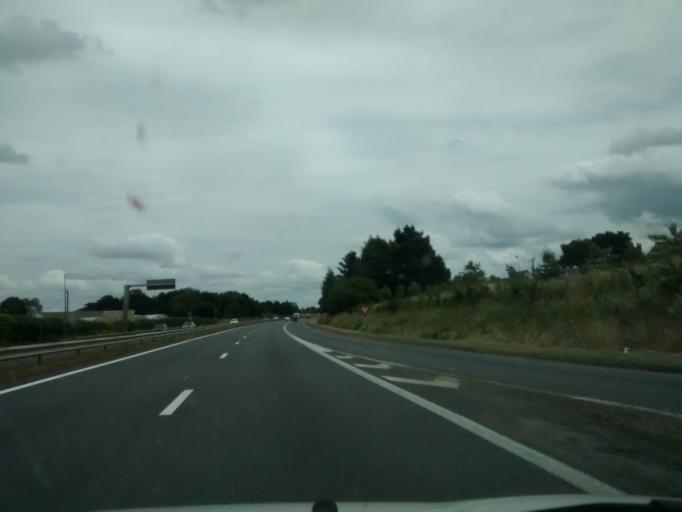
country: FR
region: Brittany
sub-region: Departement des Cotes-d'Armor
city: Plerin
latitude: 48.5441
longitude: -2.7704
